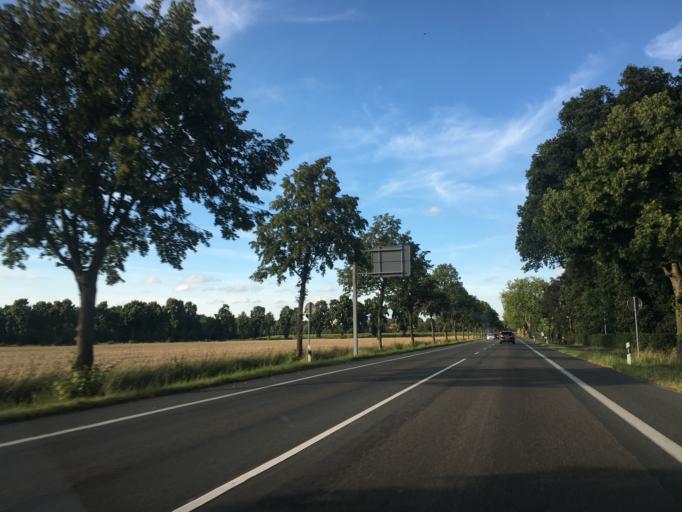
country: DE
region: North Rhine-Westphalia
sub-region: Regierungsbezirk Munster
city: Dulmen
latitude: 51.8183
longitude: 7.2614
